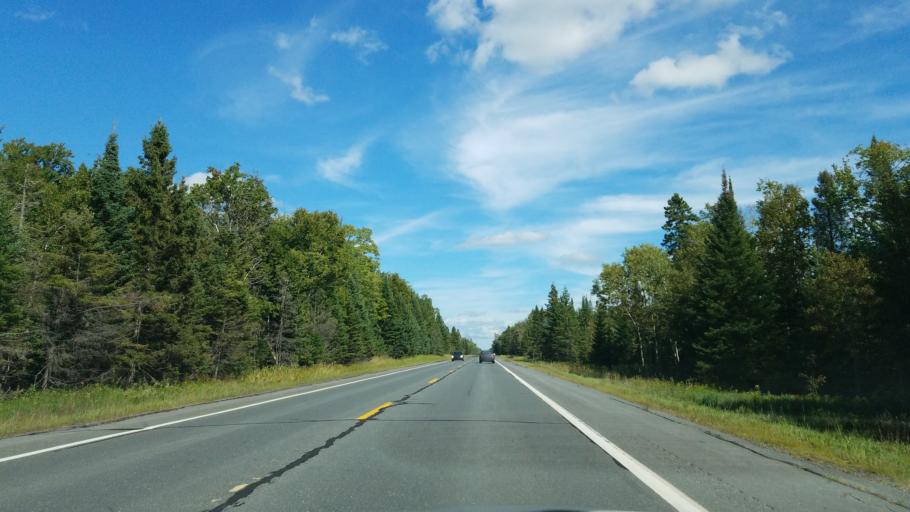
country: US
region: Michigan
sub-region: Baraga County
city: L'Anse
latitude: 46.5788
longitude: -88.4335
